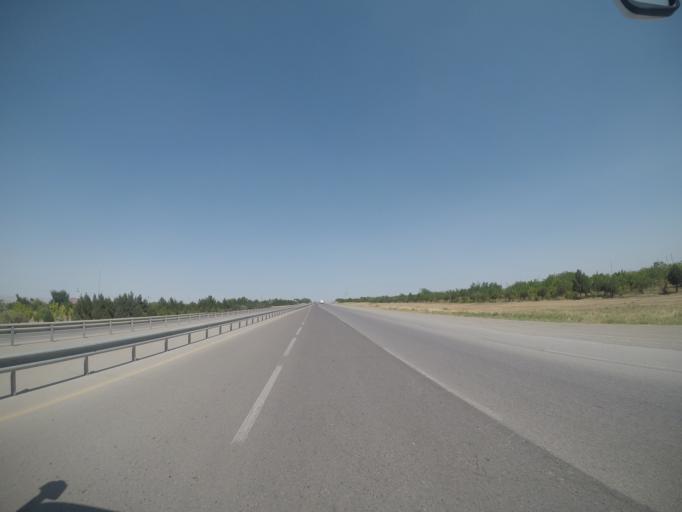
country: AZ
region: Haciqabul
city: Haciqabul
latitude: 40.0444
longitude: 49.0399
